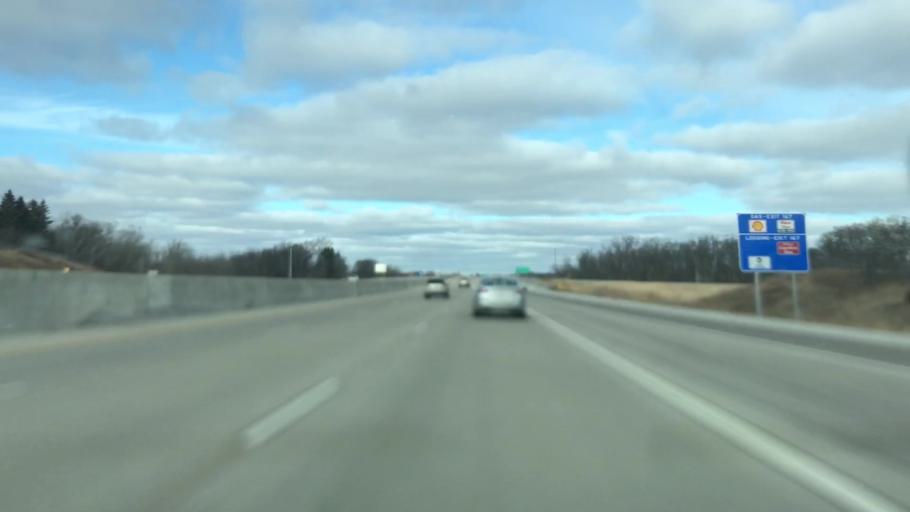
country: US
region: Wisconsin
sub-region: Brown County
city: Ashwaubenon
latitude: 44.4789
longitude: -88.0799
